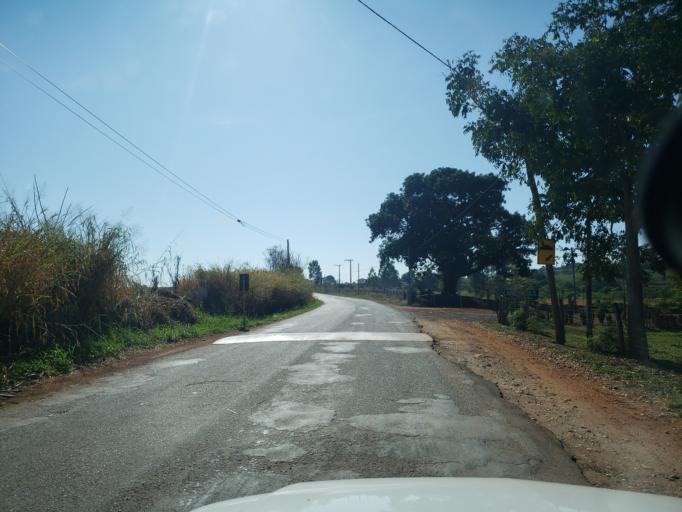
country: BR
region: Sao Paulo
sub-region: Moji-Guacu
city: Mogi-Gaucu
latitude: -22.3478
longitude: -46.8936
